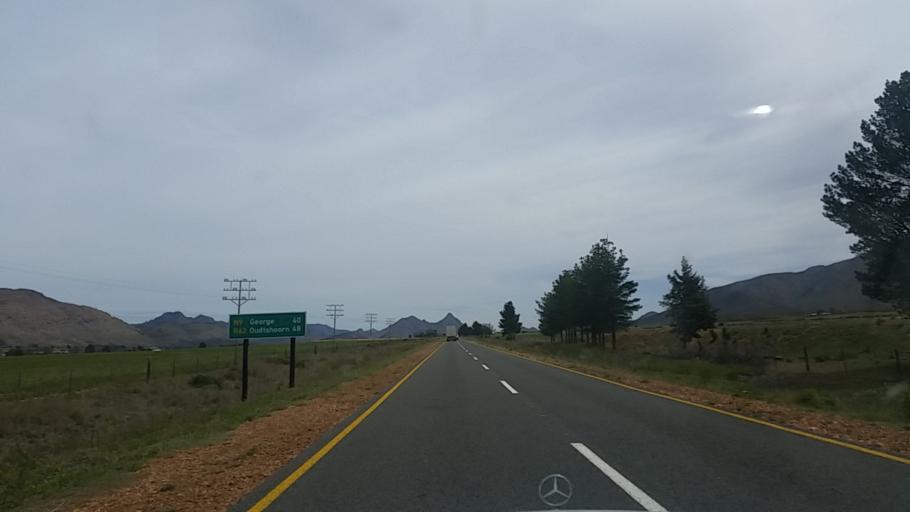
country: ZA
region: Western Cape
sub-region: Eden District Municipality
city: George
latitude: -33.8150
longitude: 22.5202
